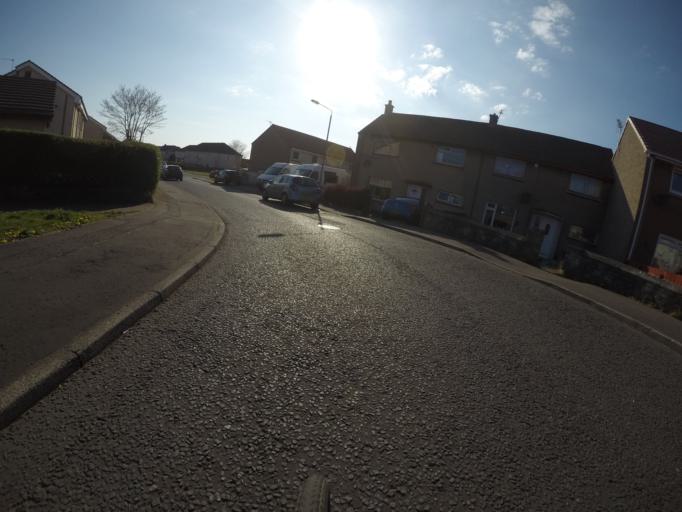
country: GB
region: Scotland
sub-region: North Ayrshire
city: Stevenston
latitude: 55.6471
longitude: -4.7471
